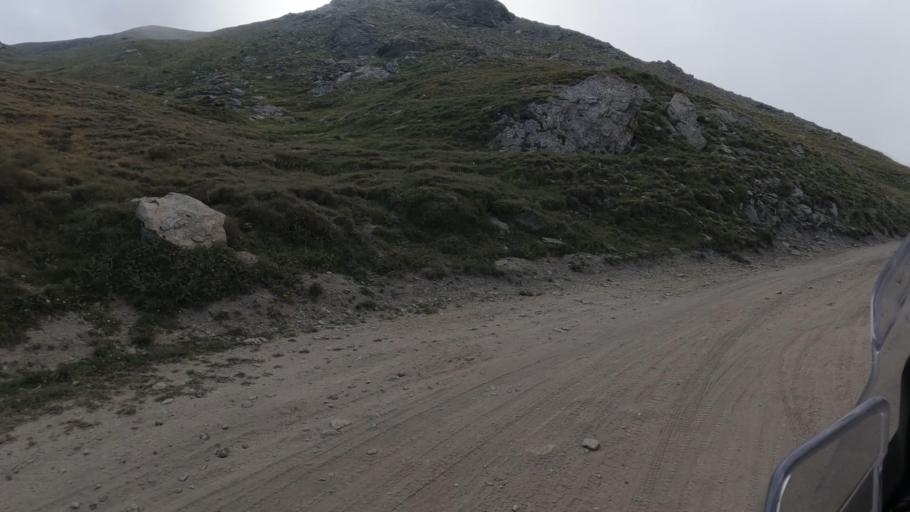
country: IT
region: Piedmont
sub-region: Provincia di Torino
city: Pragelato-Rua
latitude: 45.0494
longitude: 6.9336
